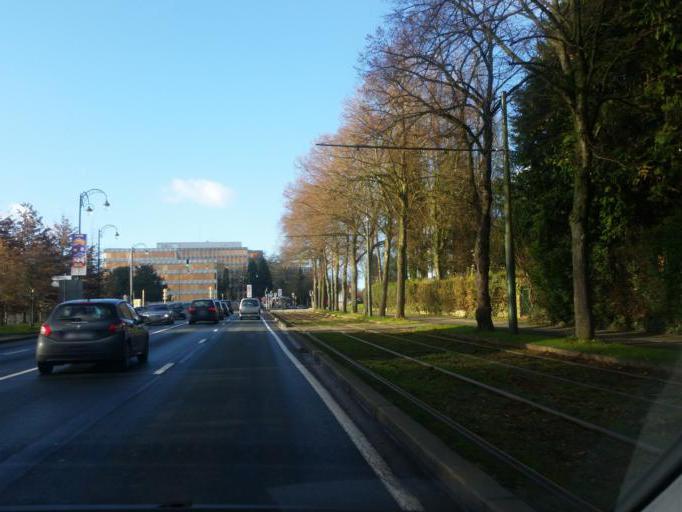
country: BE
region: Flanders
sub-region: Provincie Vlaams-Brabant
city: Hoeilaart
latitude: 50.7954
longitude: 4.4101
